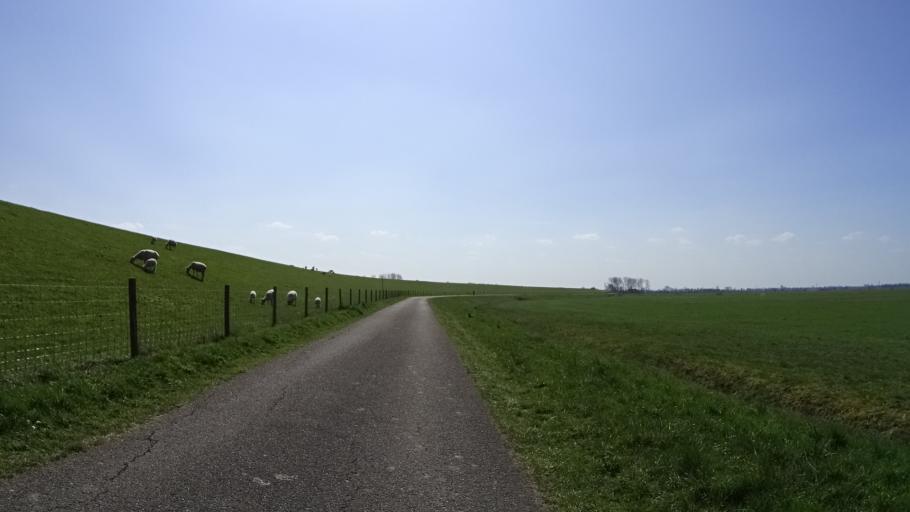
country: DE
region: Lower Saxony
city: Weener
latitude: 53.1424
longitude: 7.3693
